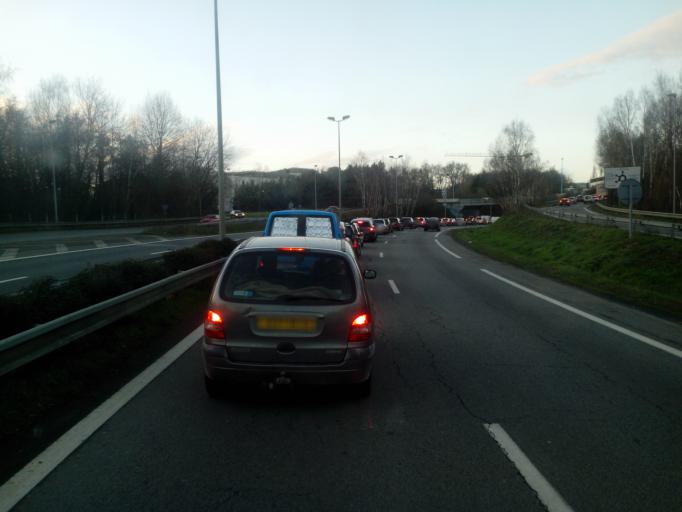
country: FR
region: Pays de la Loire
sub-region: Departement de la Loire-Atlantique
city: La Chapelle-sur-Erdre
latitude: 47.2583
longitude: -1.5551
